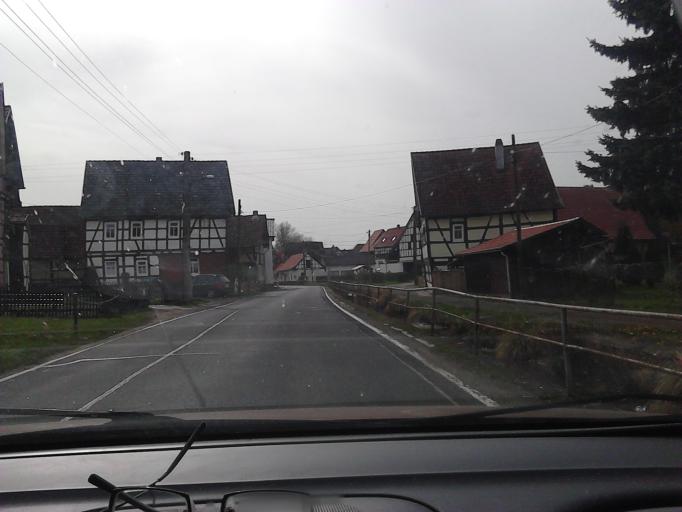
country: DE
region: Thuringia
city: Hellingen
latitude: 50.3022
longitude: 10.7518
